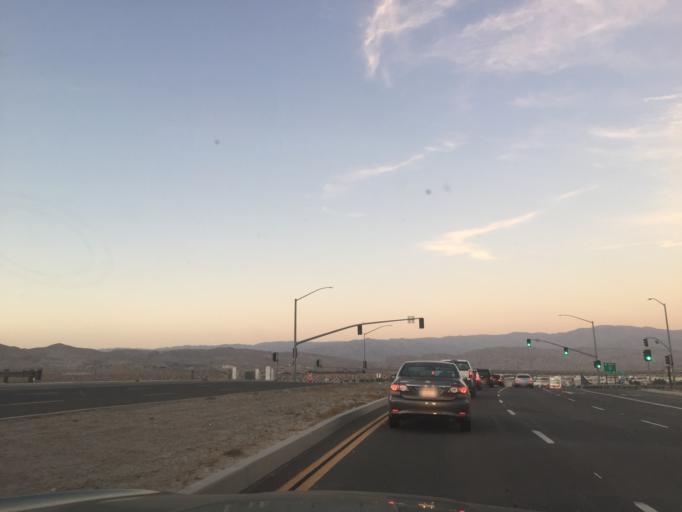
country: US
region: California
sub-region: Riverside County
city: Thousand Palms
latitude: 33.8188
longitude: -116.4102
